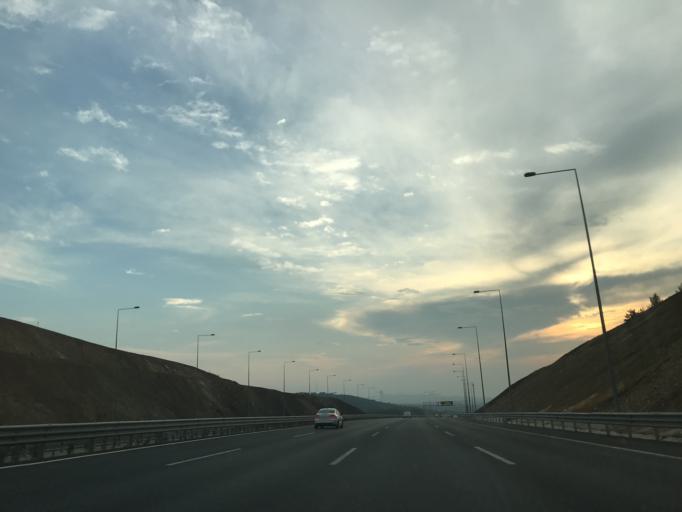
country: TR
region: Istanbul
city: Umraniye
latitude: 41.0518
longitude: 29.1651
